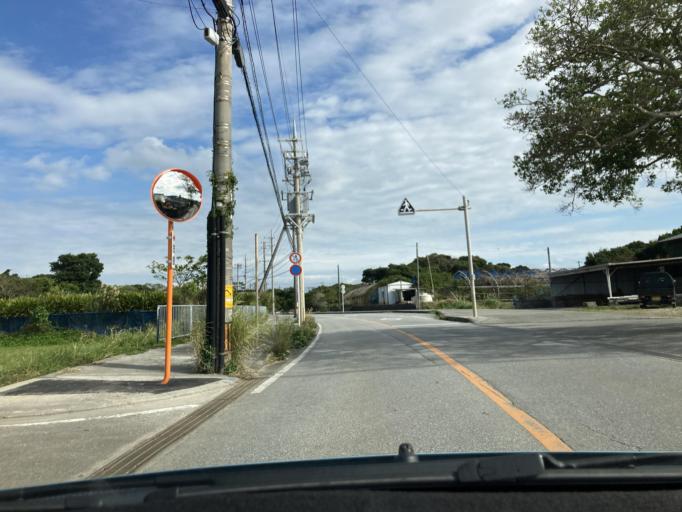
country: JP
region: Okinawa
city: Nago
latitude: 26.6914
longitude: 127.9598
